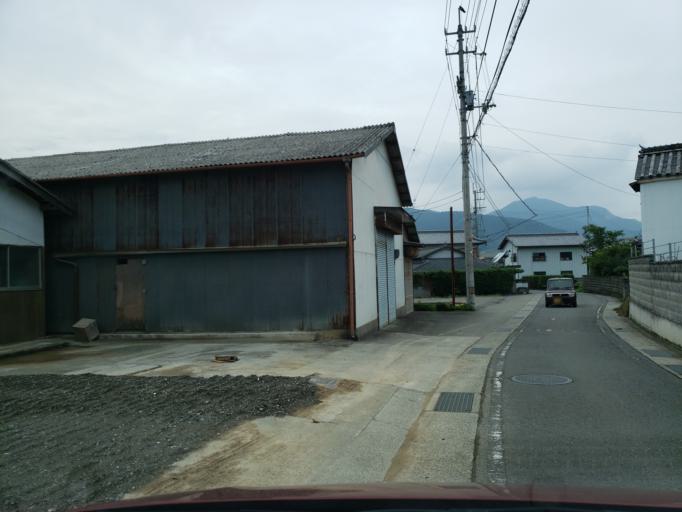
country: JP
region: Tokushima
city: Kamojimacho-jogejima
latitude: 34.1005
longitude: 134.2798
